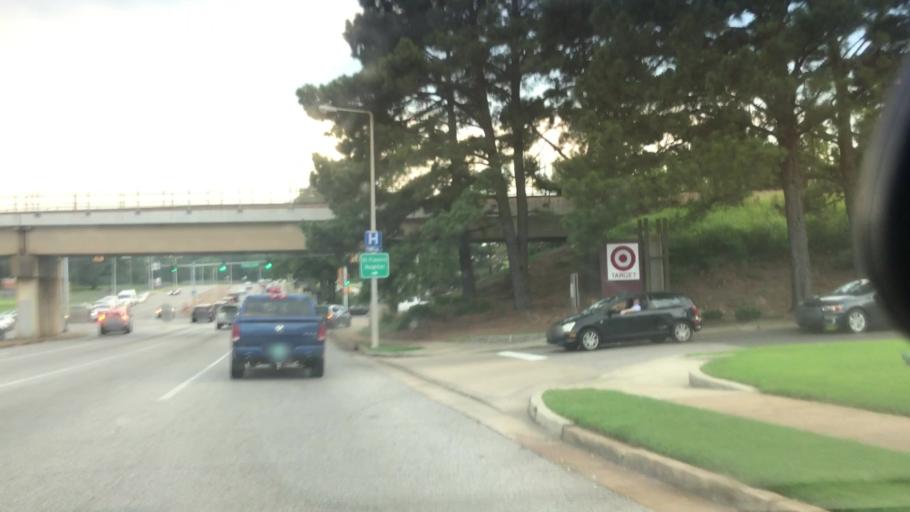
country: US
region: Tennessee
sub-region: Shelby County
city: Germantown
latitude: 35.1008
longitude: -89.8594
